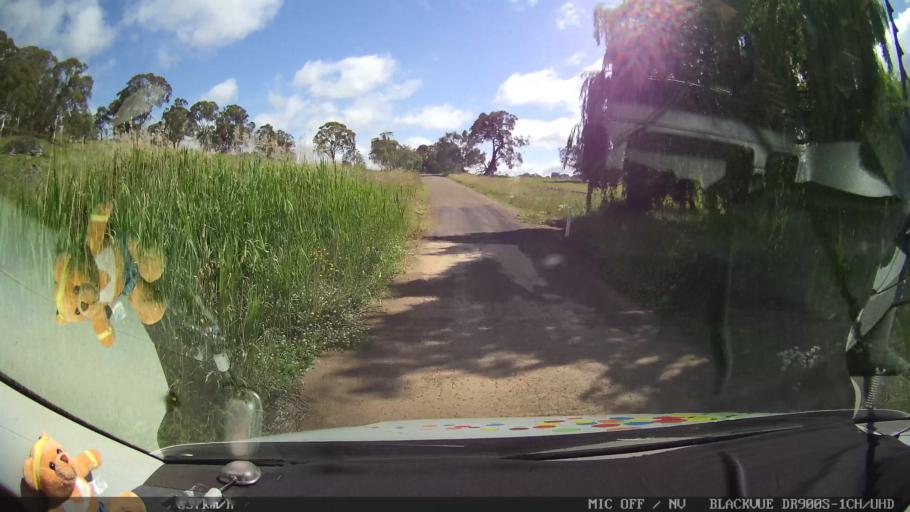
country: AU
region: New South Wales
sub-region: Guyra
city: Guyra
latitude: -29.9826
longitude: 151.6956
